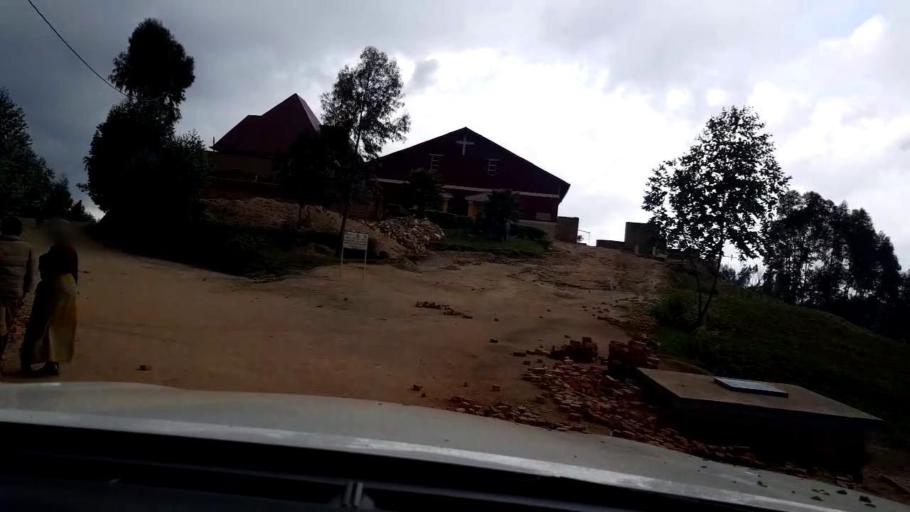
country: RW
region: Western Province
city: Kibuye
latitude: -1.8964
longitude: 29.5330
